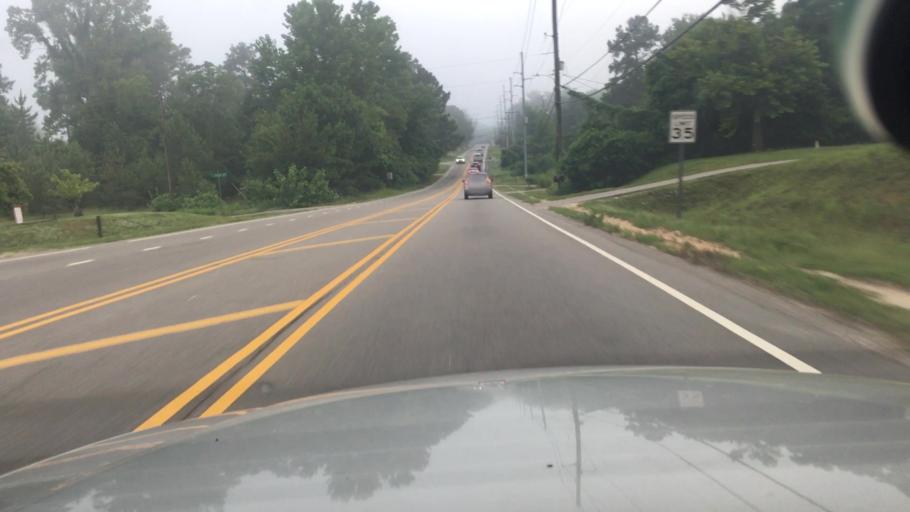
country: US
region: North Carolina
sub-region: Cumberland County
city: Hope Mills
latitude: 35.0154
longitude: -78.9400
